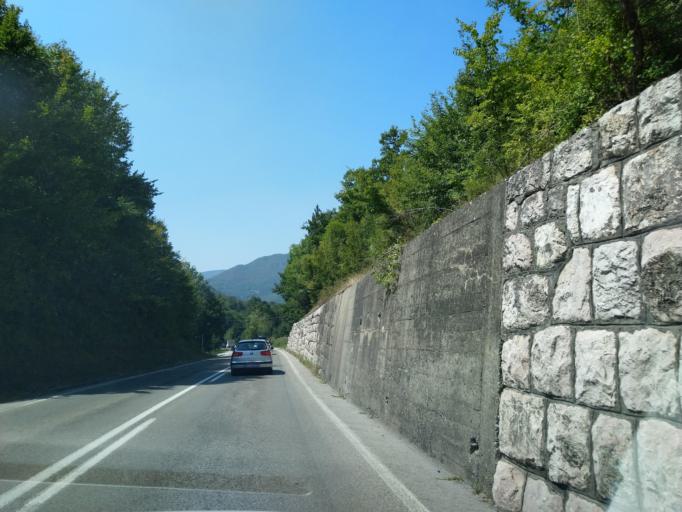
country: RS
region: Central Serbia
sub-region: Zlatiborski Okrug
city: Prijepolje
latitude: 43.4660
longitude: 19.6782
